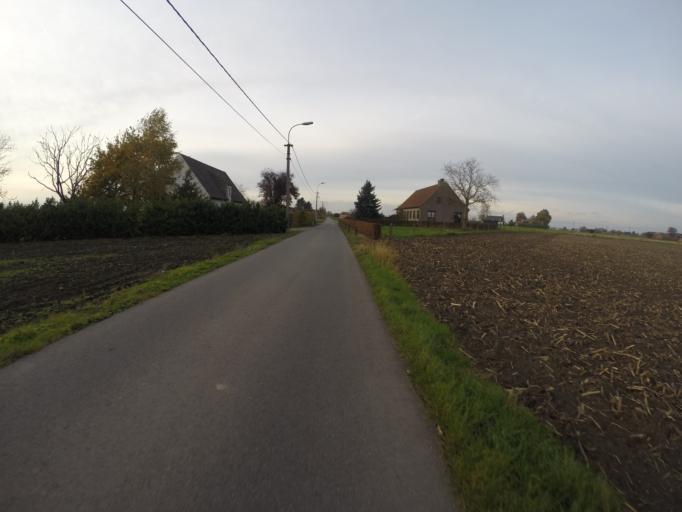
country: BE
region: Flanders
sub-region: Provincie Oost-Vlaanderen
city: Aalter
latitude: 51.0616
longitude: 3.4509
